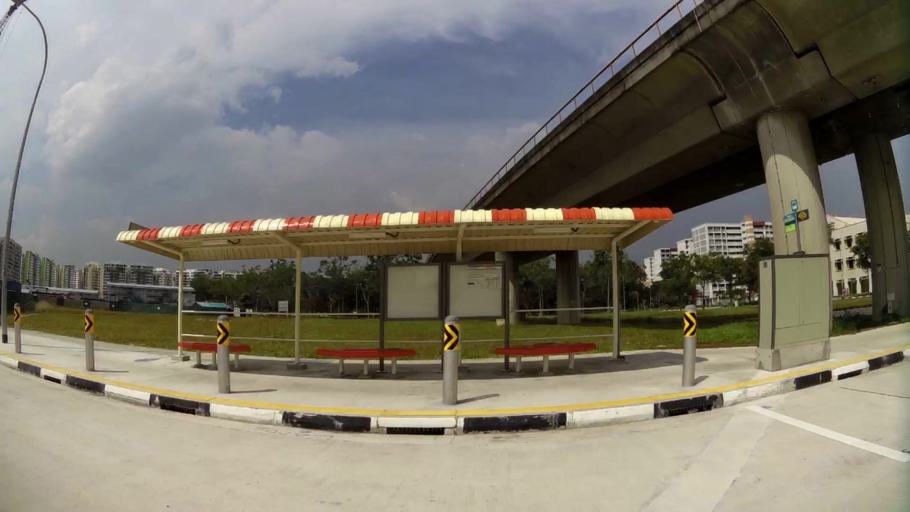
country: SG
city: Singapore
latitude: 1.3556
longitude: 103.9435
